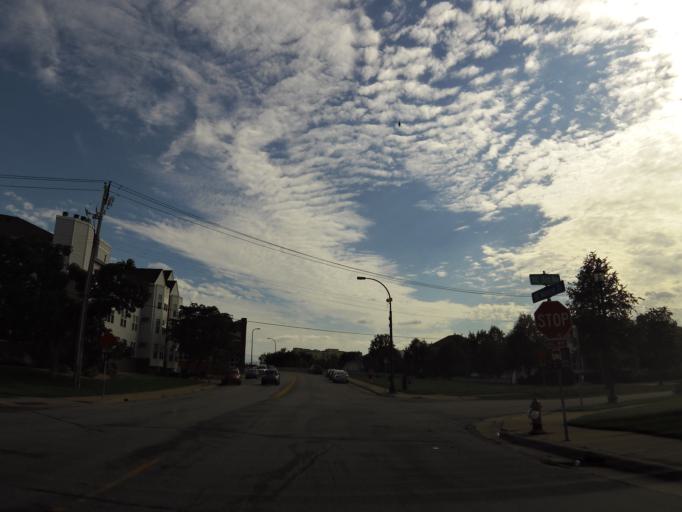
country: US
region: Minnesota
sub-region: Hennepin County
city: Minneapolis
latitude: 44.9935
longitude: -93.2525
